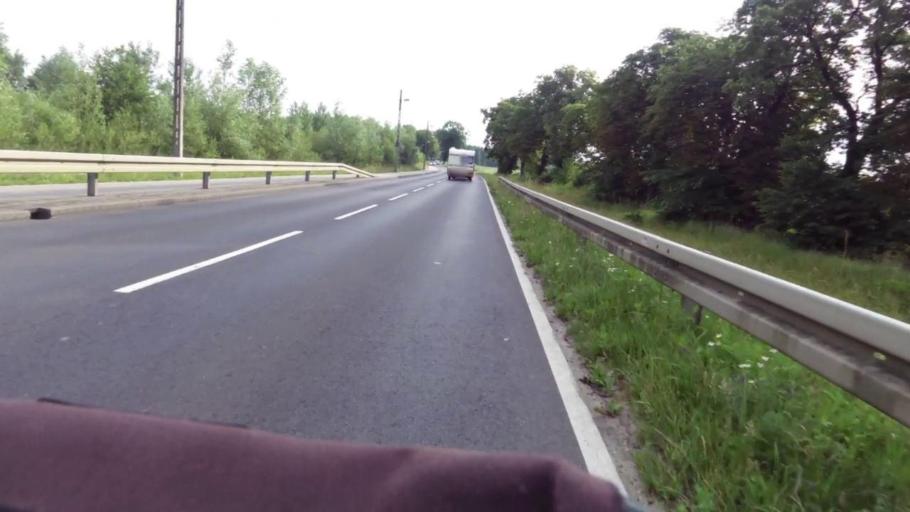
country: PL
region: West Pomeranian Voivodeship
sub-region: Powiat kamienski
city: Kamien Pomorski
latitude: 53.9732
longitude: 14.7870
